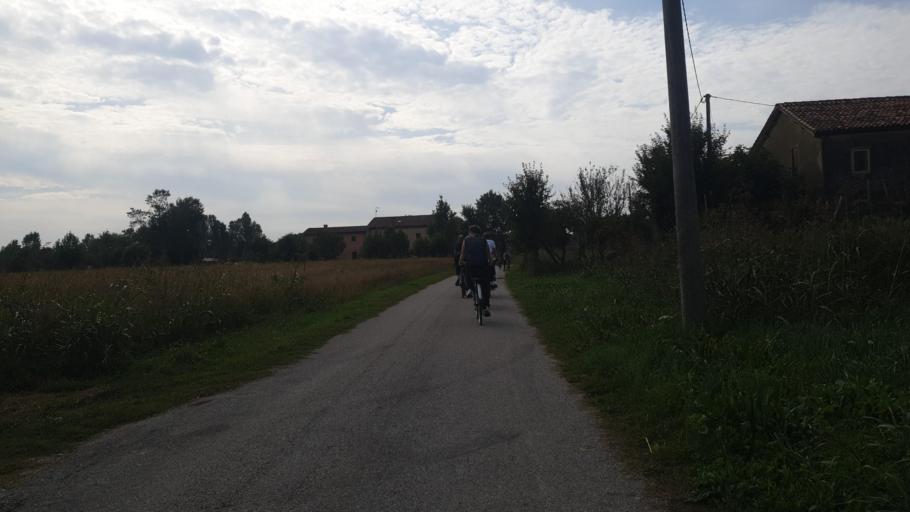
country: IT
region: Veneto
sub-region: Provincia di Padova
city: Cervarese Santa Croce
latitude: 45.4146
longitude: 11.6971
